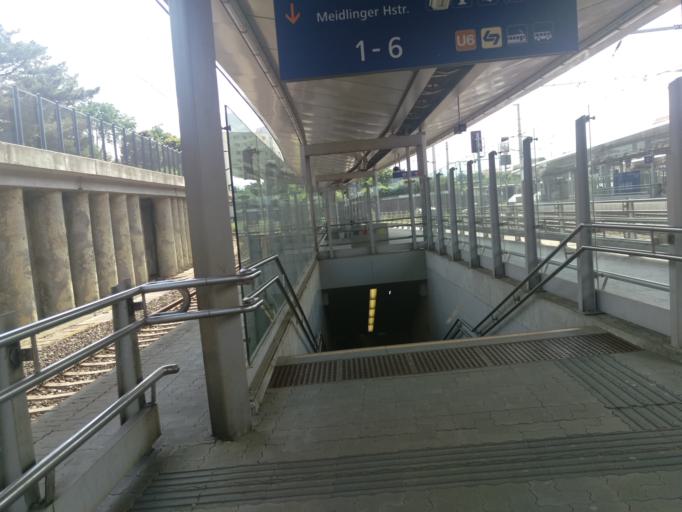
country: AT
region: Vienna
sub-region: Wien Stadt
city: Vienna
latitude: 48.1741
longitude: 16.3335
